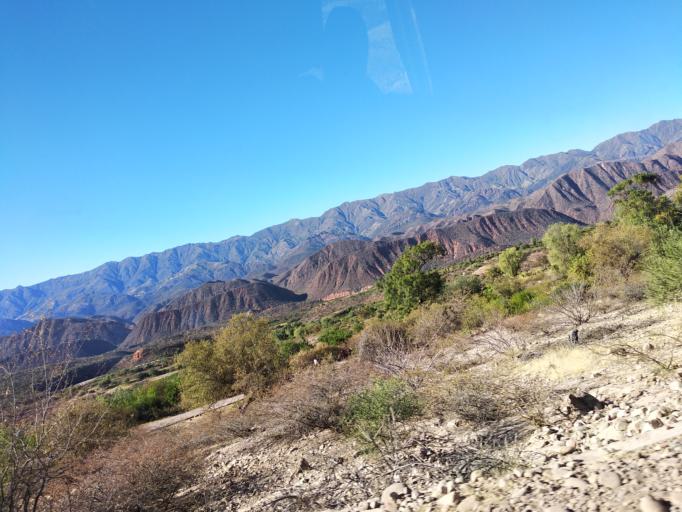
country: BO
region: Cochabamba
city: Mizque
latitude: -18.0812
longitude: -65.7462
